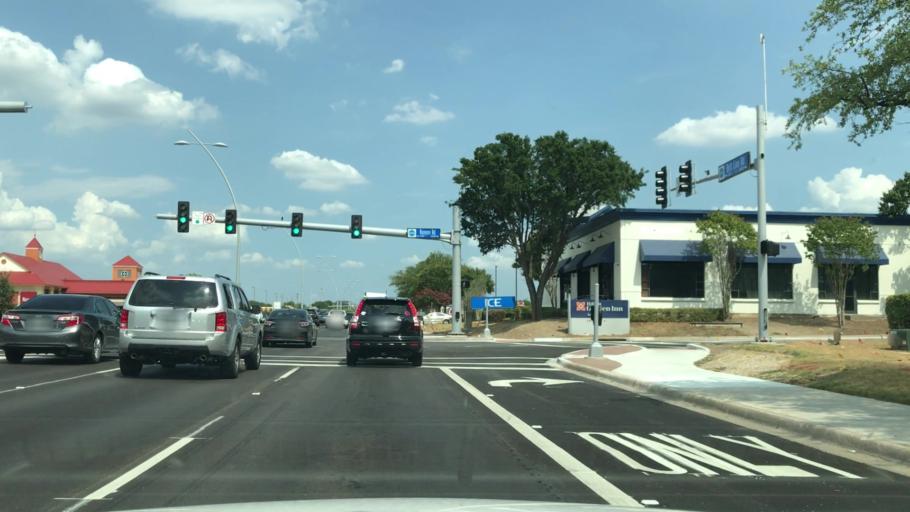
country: US
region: Texas
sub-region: Dallas County
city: Addison
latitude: 32.9543
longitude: -96.8440
